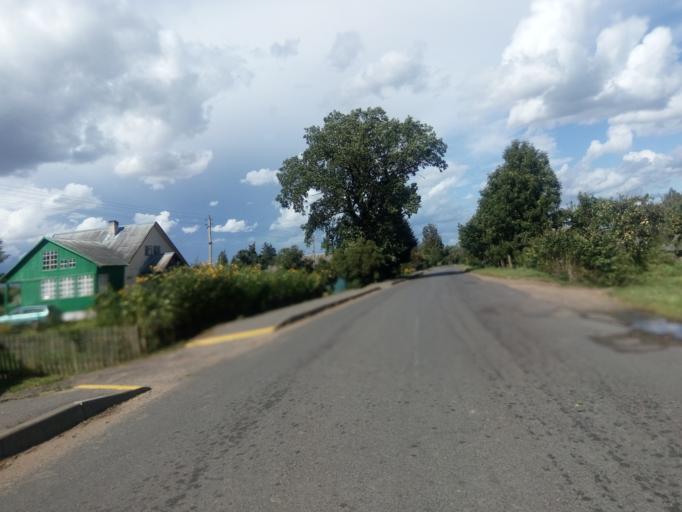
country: BY
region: Vitebsk
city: Dzisna
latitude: 55.7112
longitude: 28.1872
